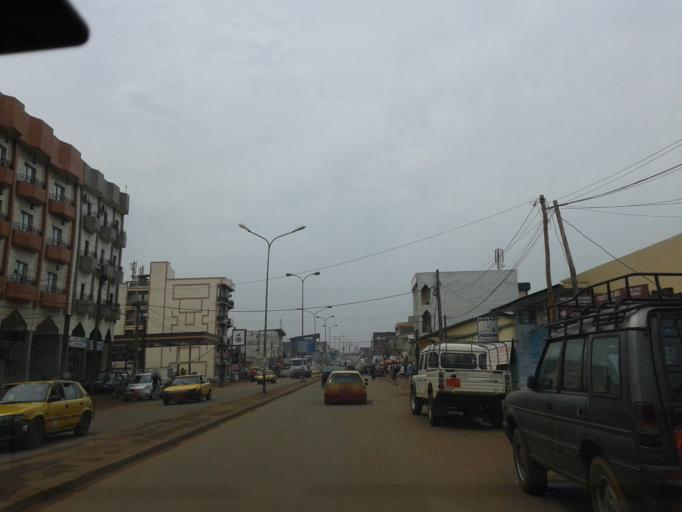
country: CM
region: Centre
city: Yaounde
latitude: 3.8617
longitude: 11.5237
